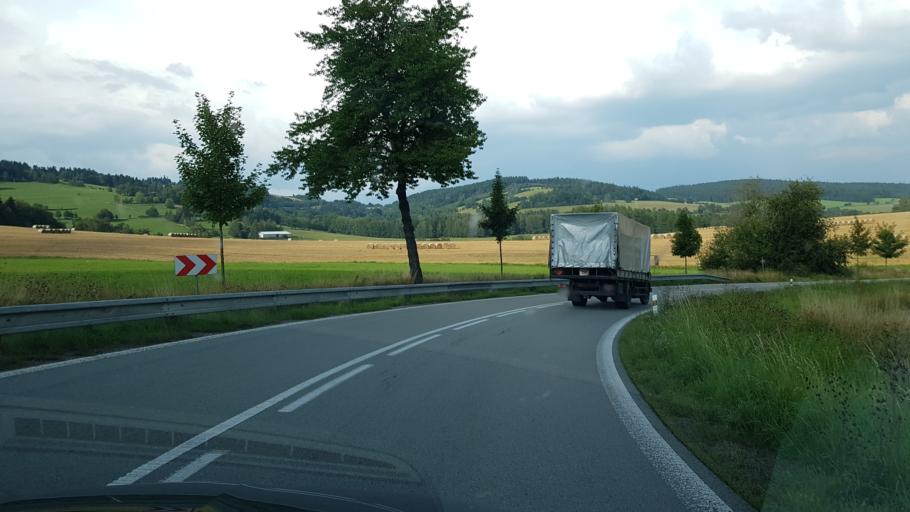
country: CZ
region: Pardubicky
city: Jablonne nad Orlici
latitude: 50.0965
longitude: 16.6155
